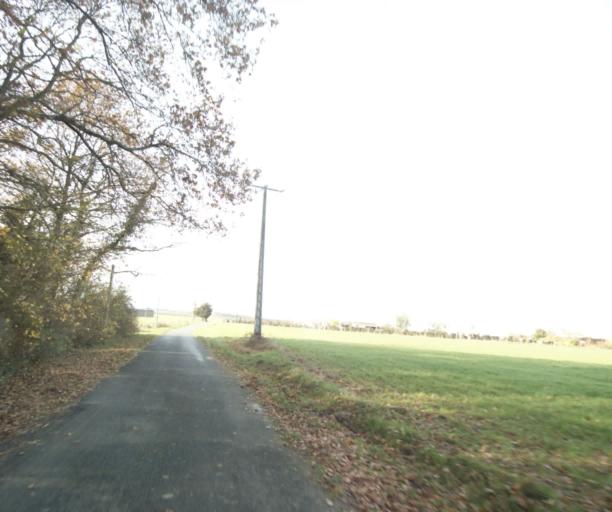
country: FR
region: Poitou-Charentes
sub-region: Departement de la Charente-Maritime
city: Chaniers
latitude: 45.7403
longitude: -0.5162
